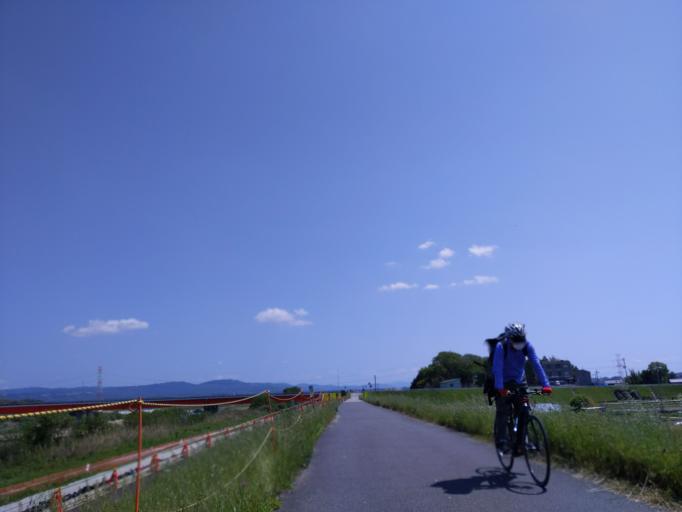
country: JP
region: Kyoto
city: Tanabe
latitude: 34.7708
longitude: 135.8012
